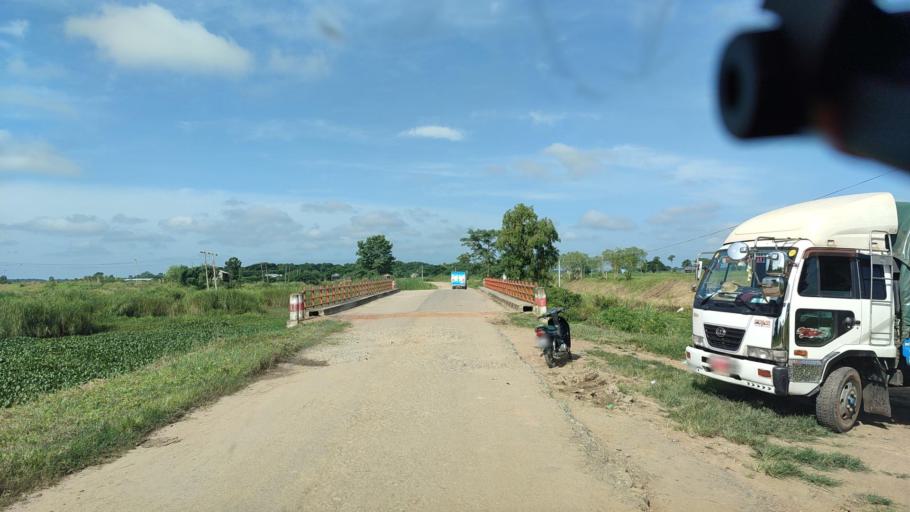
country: MM
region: Bago
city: Letpandan
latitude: 17.7619
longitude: 95.6810
